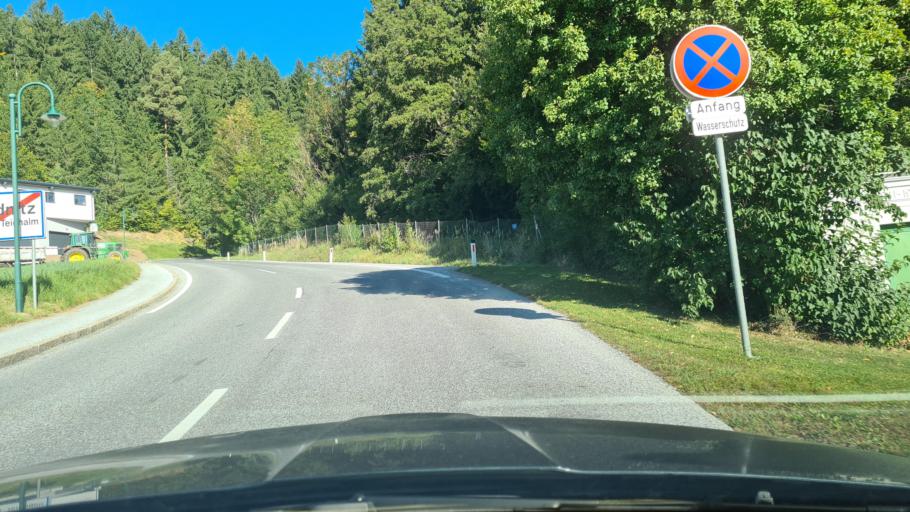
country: AT
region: Styria
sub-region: Politischer Bezirk Weiz
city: Passail
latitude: 47.2899
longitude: 15.4763
